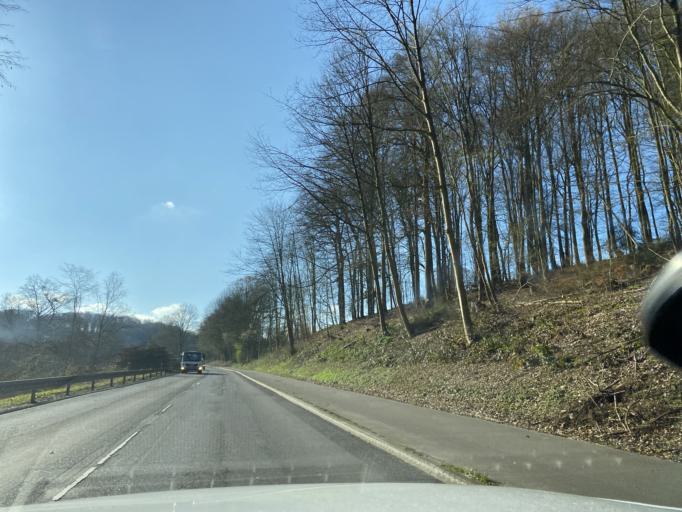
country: DE
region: North Rhine-Westphalia
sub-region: Regierungsbezirk Koln
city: Odenthal
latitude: 51.0244
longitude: 7.1236
